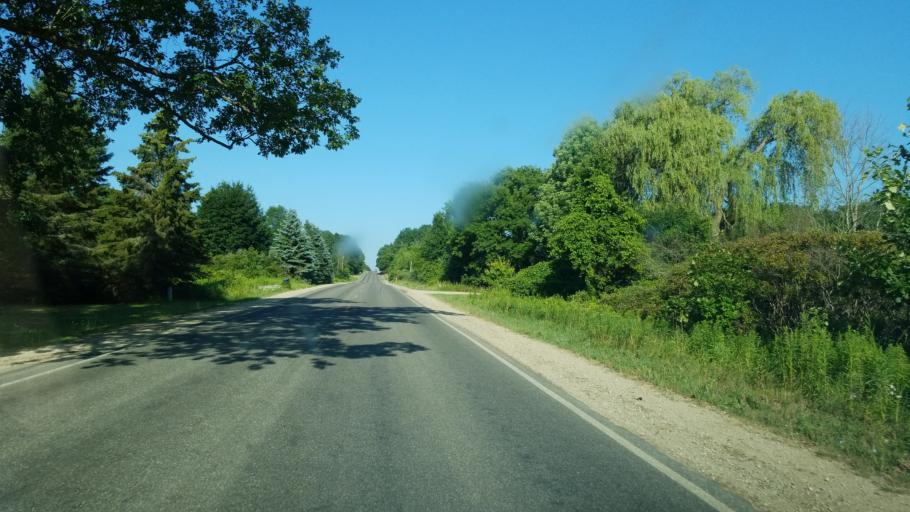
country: US
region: Michigan
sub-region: Montcalm County
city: Howard City
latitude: 43.4899
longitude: -85.4649
